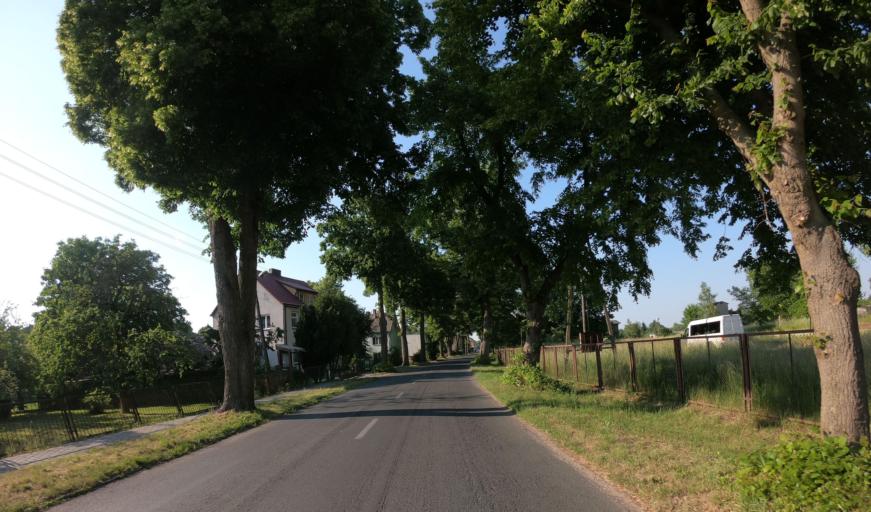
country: PL
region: West Pomeranian Voivodeship
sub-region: Powiat lobeski
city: Dobra
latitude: 53.5774
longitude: 15.3047
